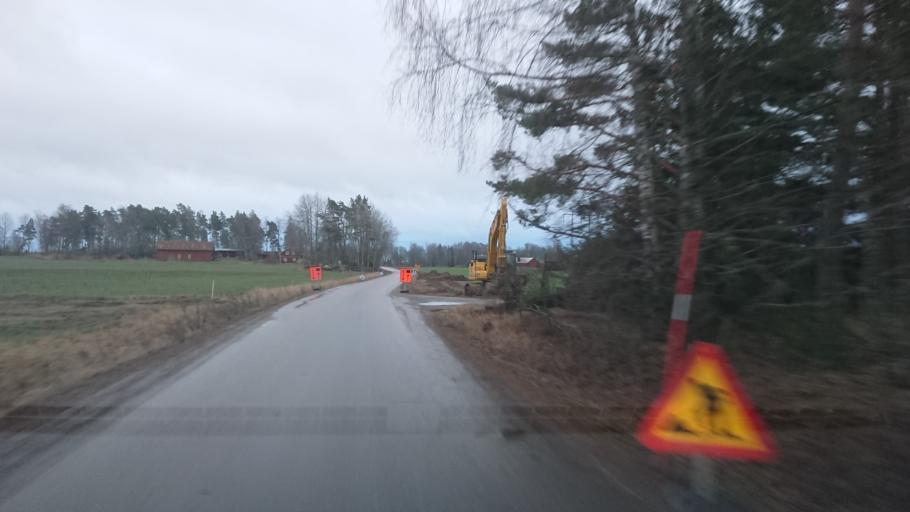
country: SE
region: Uppsala
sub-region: Uppsala Kommun
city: Gamla Uppsala
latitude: 59.9622
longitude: 17.6031
